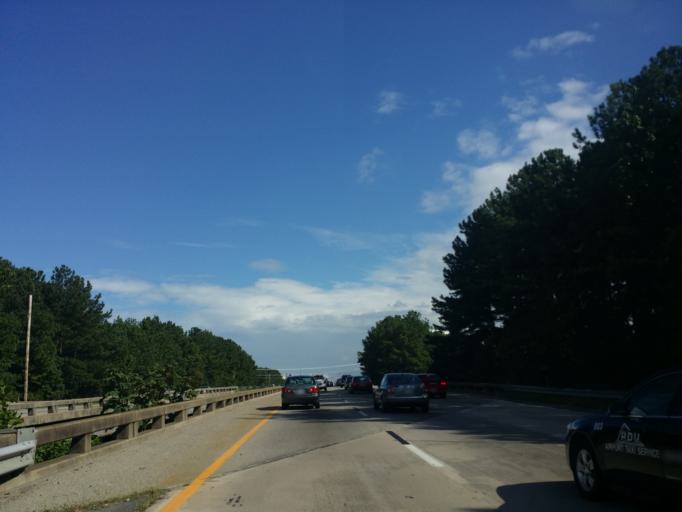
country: US
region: North Carolina
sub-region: Durham County
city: Durham
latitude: 35.9728
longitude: -78.8708
